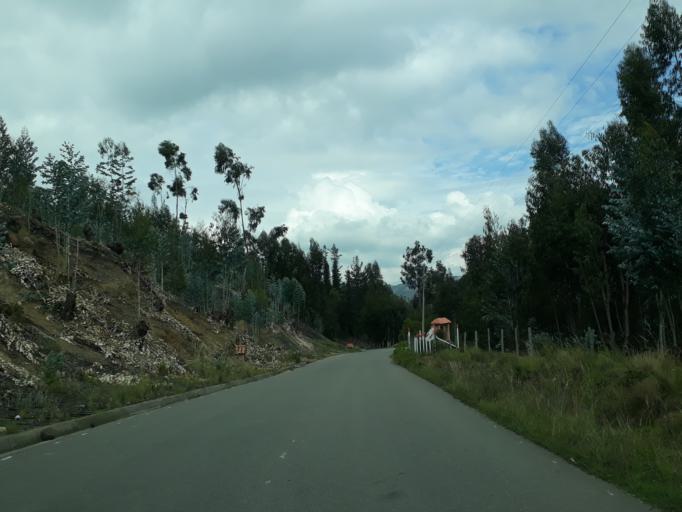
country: CO
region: Cundinamarca
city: Suesca
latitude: 5.0842
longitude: -73.7864
